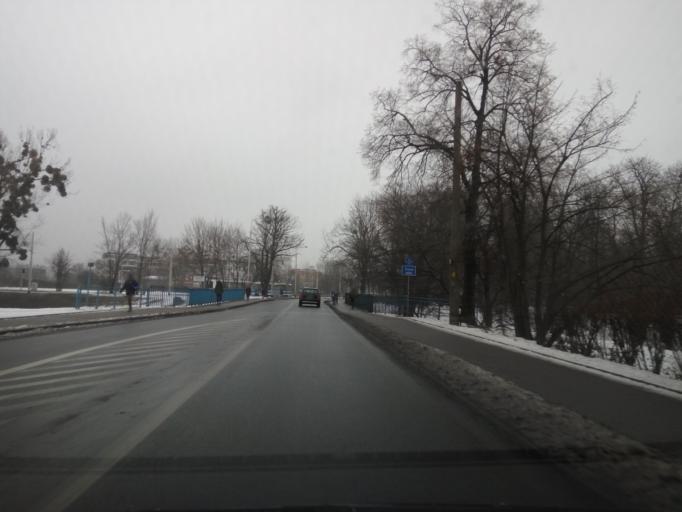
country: PL
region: Lower Silesian Voivodeship
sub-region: Powiat wroclawski
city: Bielany Wroclawskie
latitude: 51.0646
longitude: 16.9854
